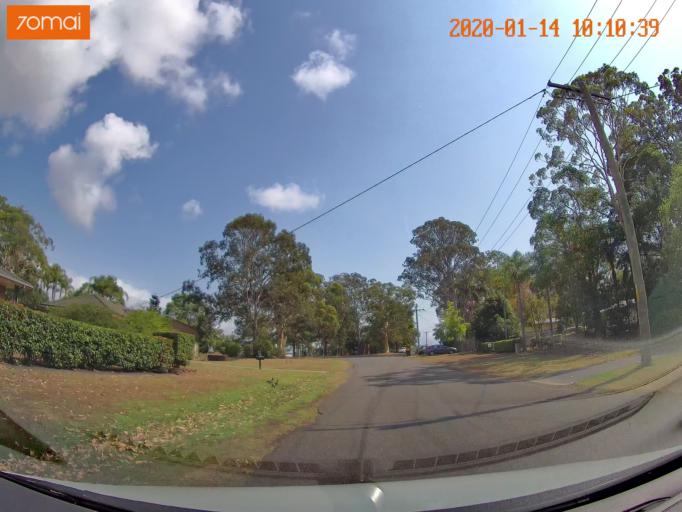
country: AU
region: New South Wales
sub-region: Wyong Shire
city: Kingfisher Shores
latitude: -33.1215
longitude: 151.5360
